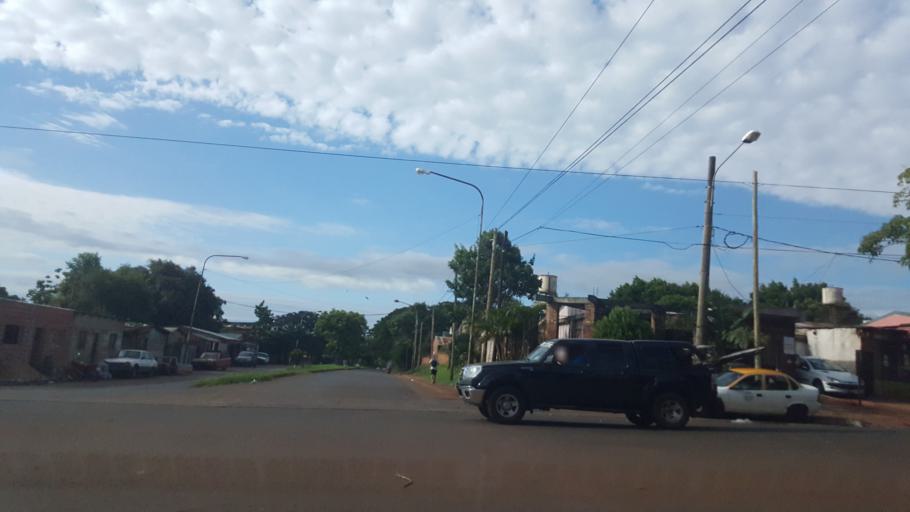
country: AR
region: Misiones
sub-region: Departamento de Capital
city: Posadas
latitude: -27.3808
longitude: -55.9335
